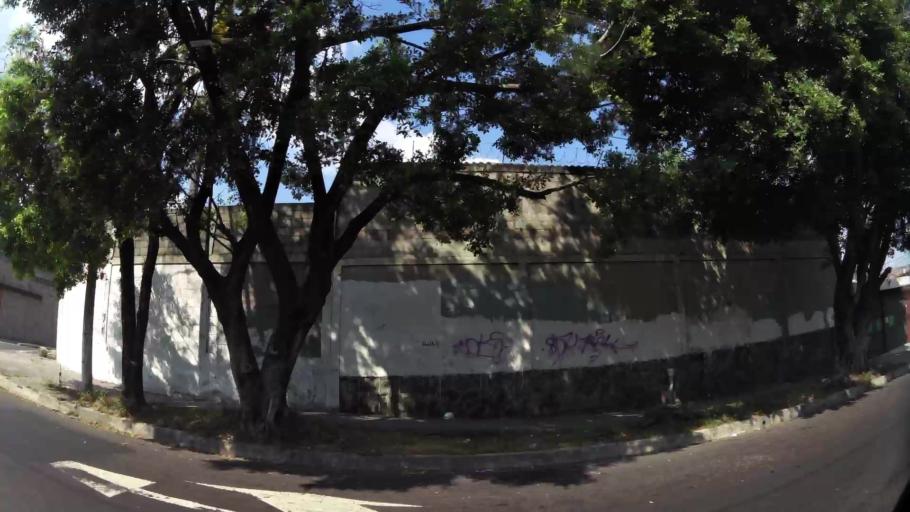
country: SV
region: San Salvador
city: Mejicanos
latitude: 13.7233
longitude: -89.2157
